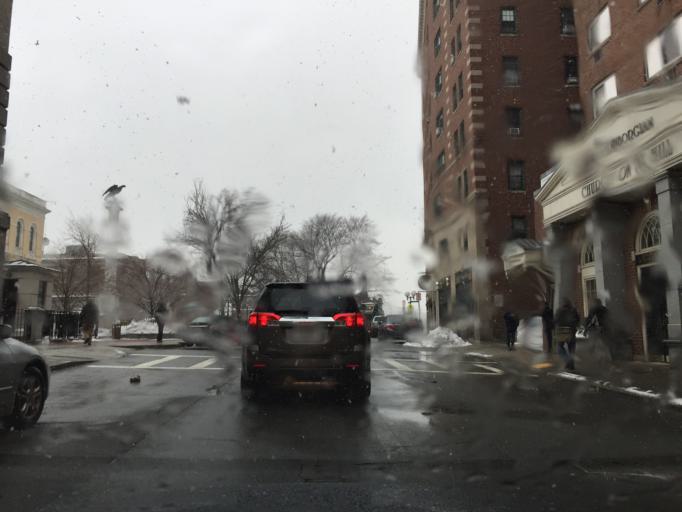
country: US
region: Massachusetts
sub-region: Suffolk County
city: Boston
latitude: 42.3585
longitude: -71.0628
